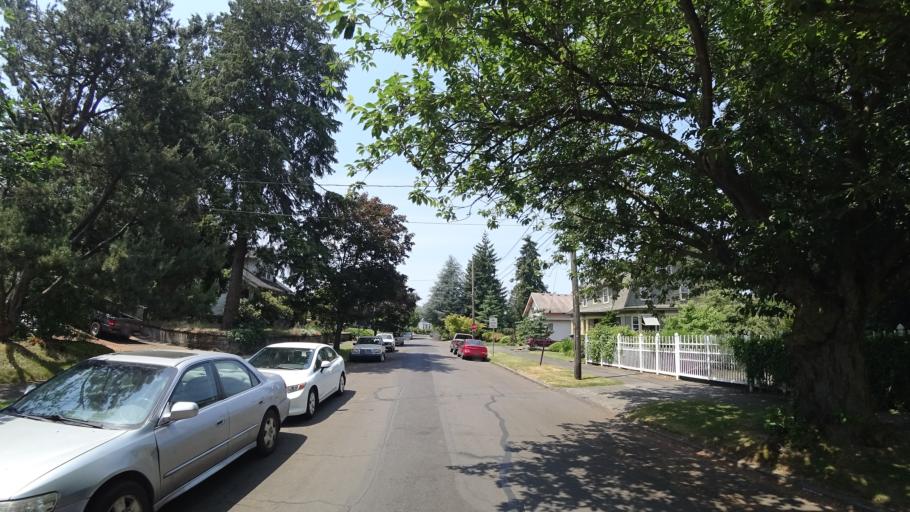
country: US
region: Oregon
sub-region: Multnomah County
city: Portland
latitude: 45.5781
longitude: -122.6851
